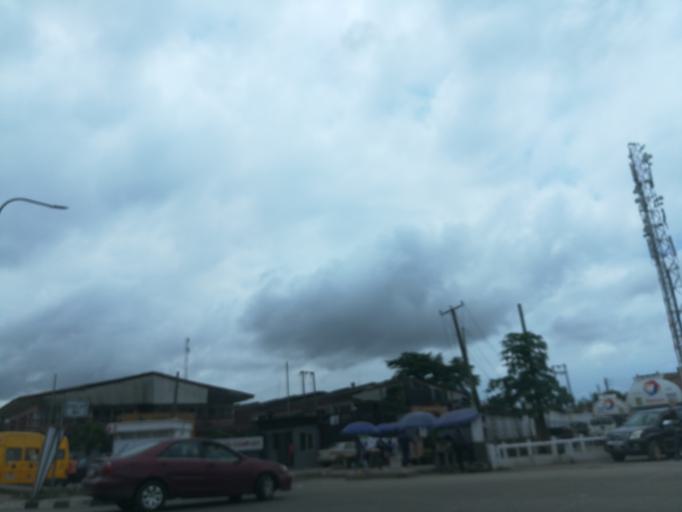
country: NG
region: Lagos
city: Lagos
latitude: 6.4546
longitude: 3.4032
